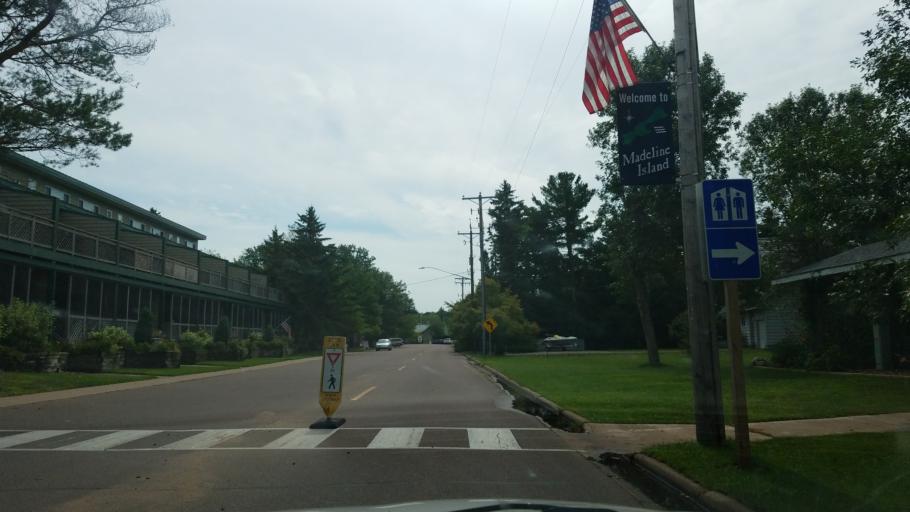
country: US
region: Wisconsin
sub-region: Bayfield County
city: Washburn
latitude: 46.7751
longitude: -90.7833
